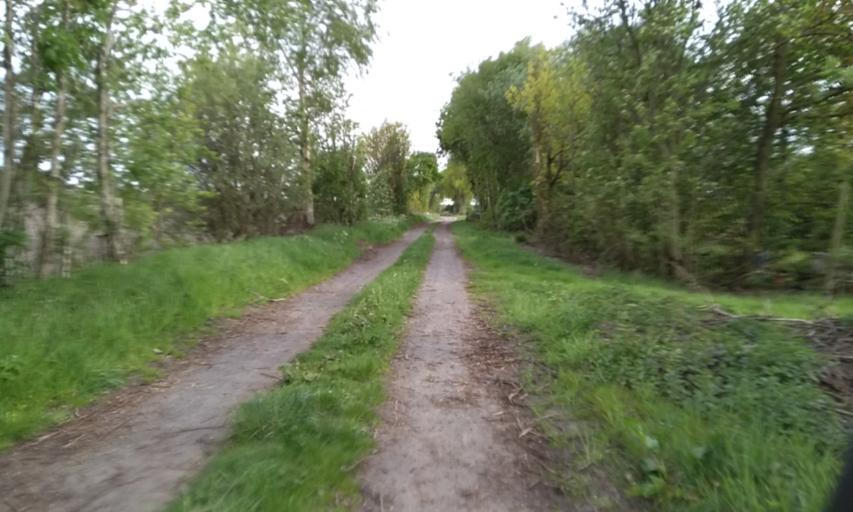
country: DE
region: Lower Saxony
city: Apensen
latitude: 53.4375
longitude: 9.5914
